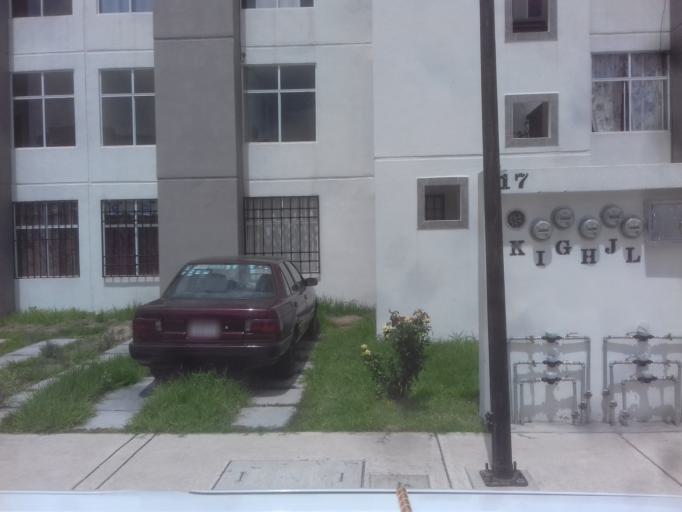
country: MX
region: Aguascalientes
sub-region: Aguascalientes
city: San Sebastian [Fraccionamiento]
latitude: 21.8079
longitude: -102.2701
